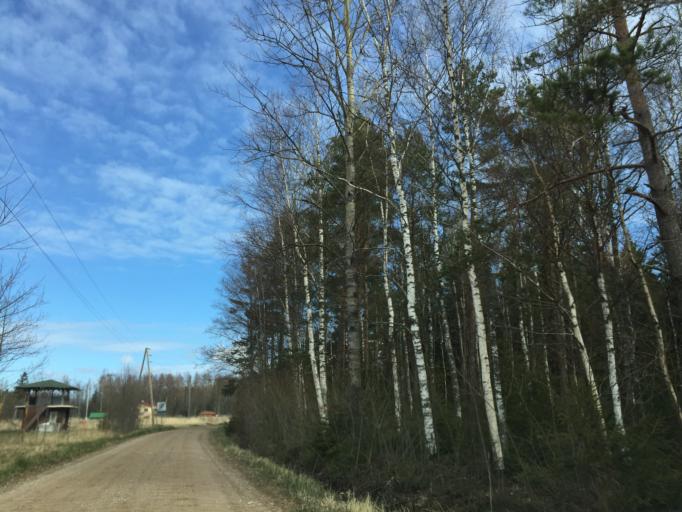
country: LV
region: Salacgrivas
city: Salacgriva
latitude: 57.6132
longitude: 24.3894
